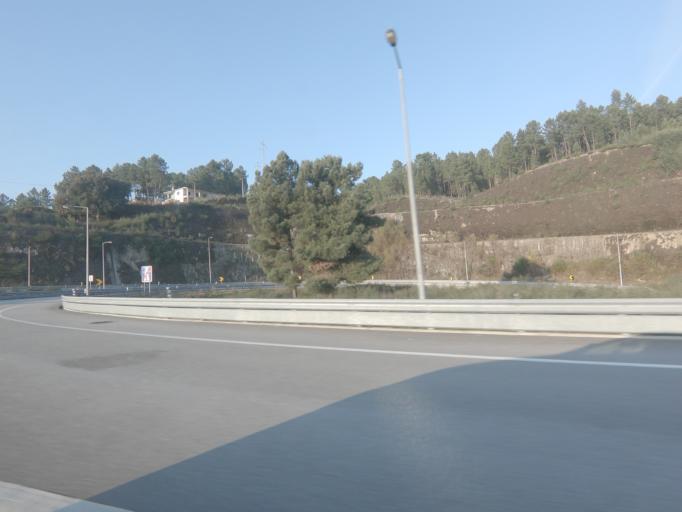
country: PT
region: Porto
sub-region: Amarante
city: Amarante
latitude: 41.2559
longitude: -8.0473
